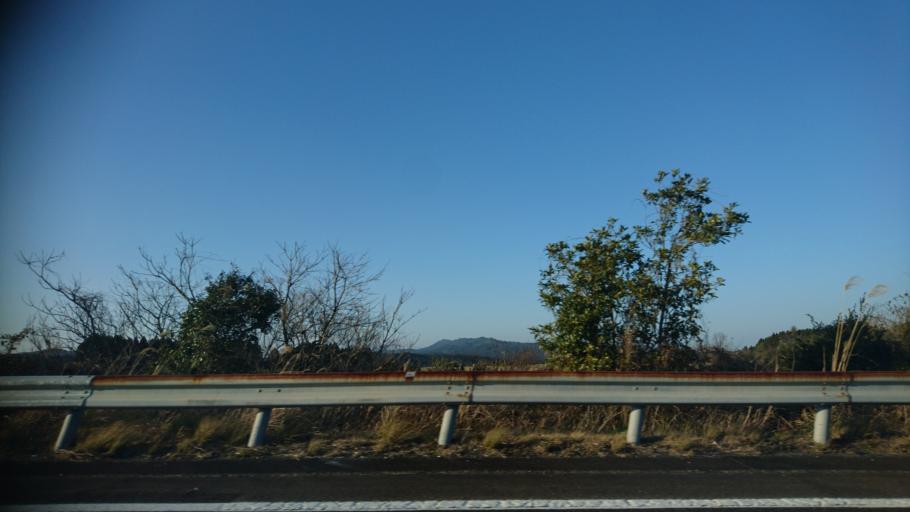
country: JP
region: Miyazaki
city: Miyazaki-shi
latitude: 31.8206
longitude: 131.2829
